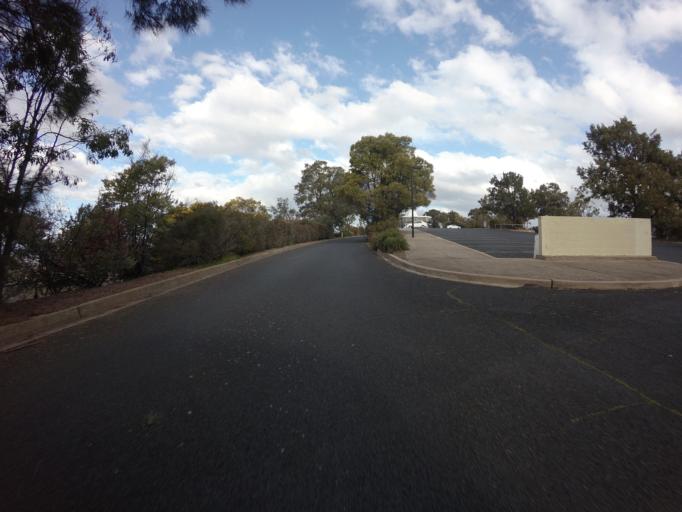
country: AU
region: Australian Capital Territory
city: Forrest
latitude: -35.3275
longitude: 149.1163
